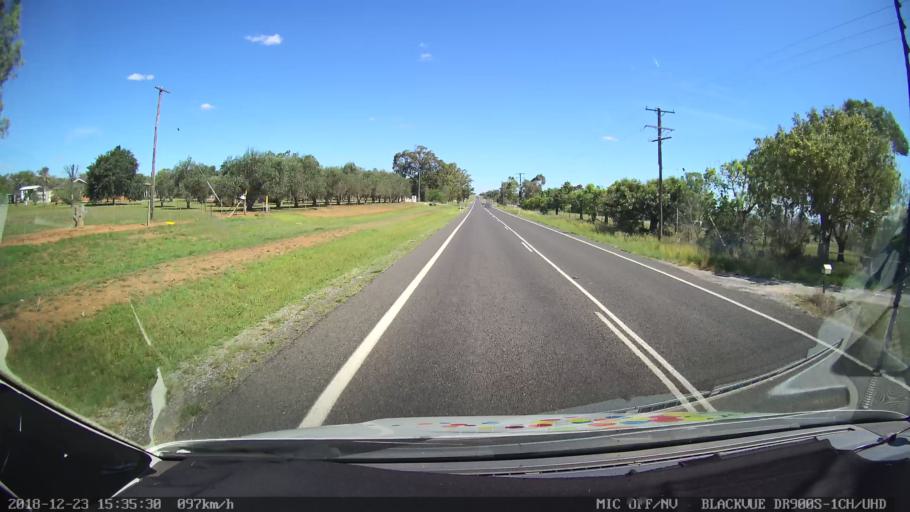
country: AU
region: New South Wales
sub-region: Tamworth Municipality
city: Tamworth
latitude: -31.0283
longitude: 150.8828
